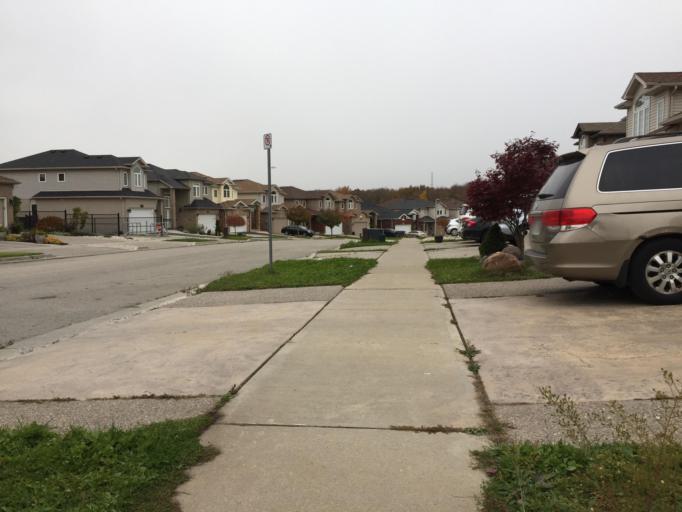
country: CA
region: Ontario
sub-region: Wellington County
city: Guelph
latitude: 43.5215
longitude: -80.3052
